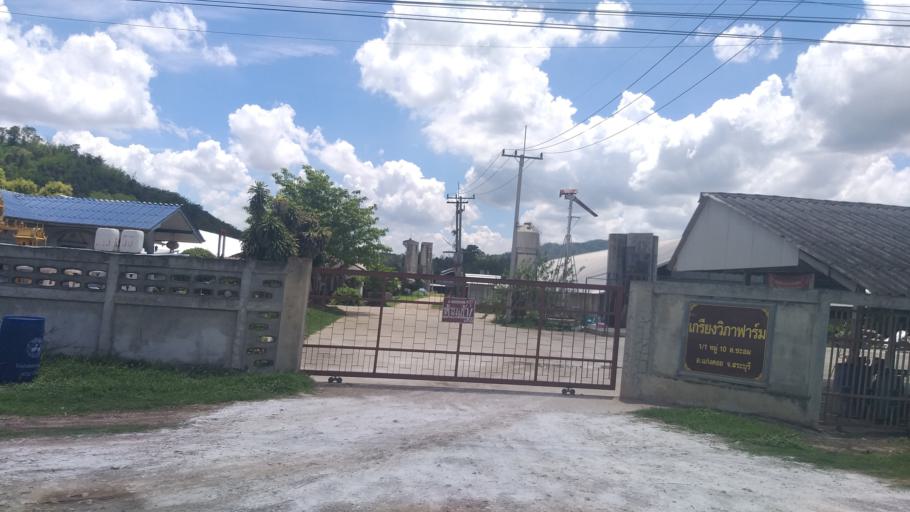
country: TH
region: Sara Buri
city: Wihan Daeng
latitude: 14.3892
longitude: 101.0955
